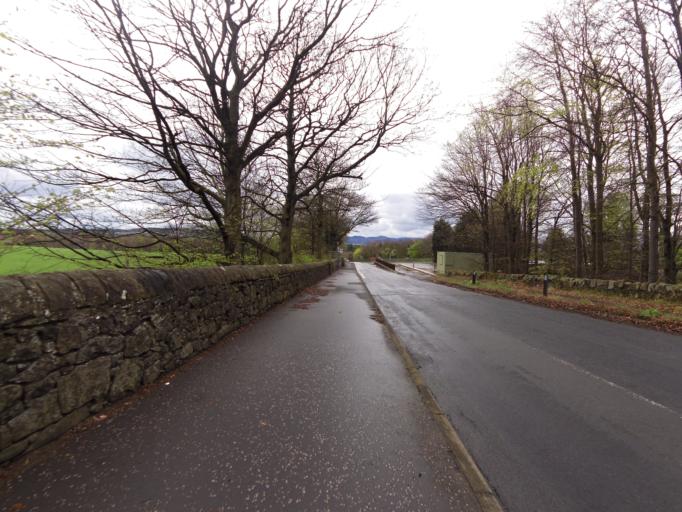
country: GB
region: Scotland
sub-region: Edinburgh
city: Currie
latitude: 55.9685
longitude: -3.3220
